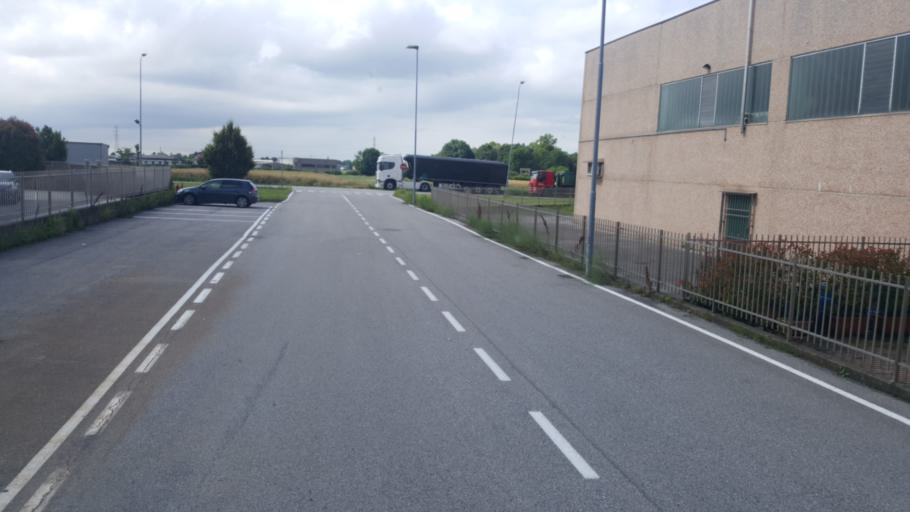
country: IT
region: Lombardy
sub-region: Provincia di Varese
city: Gerenzano
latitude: 45.6302
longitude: 9.0107
